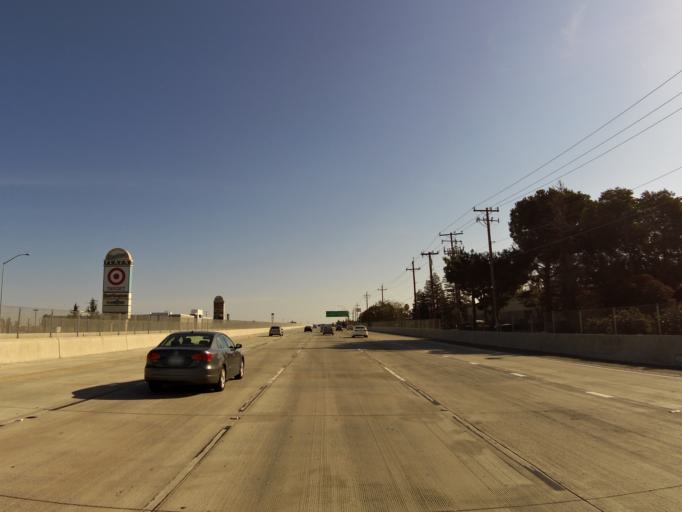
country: US
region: California
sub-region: Contra Costa County
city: Antioch
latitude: 38.0056
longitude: -121.8441
